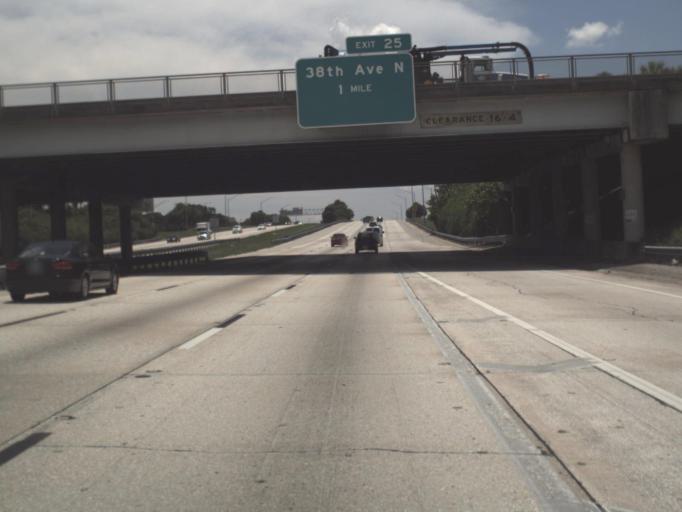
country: US
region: Florida
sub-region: Pinellas County
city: Lealman
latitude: 27.8217
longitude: -82.6649
